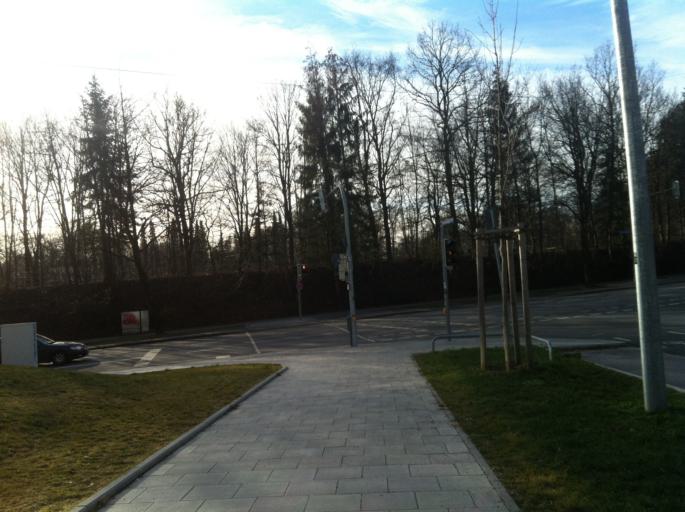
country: DE
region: Bavaria
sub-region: Upper Bavaria
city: Pullach im Isartal
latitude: 48.0908
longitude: 11.5297
